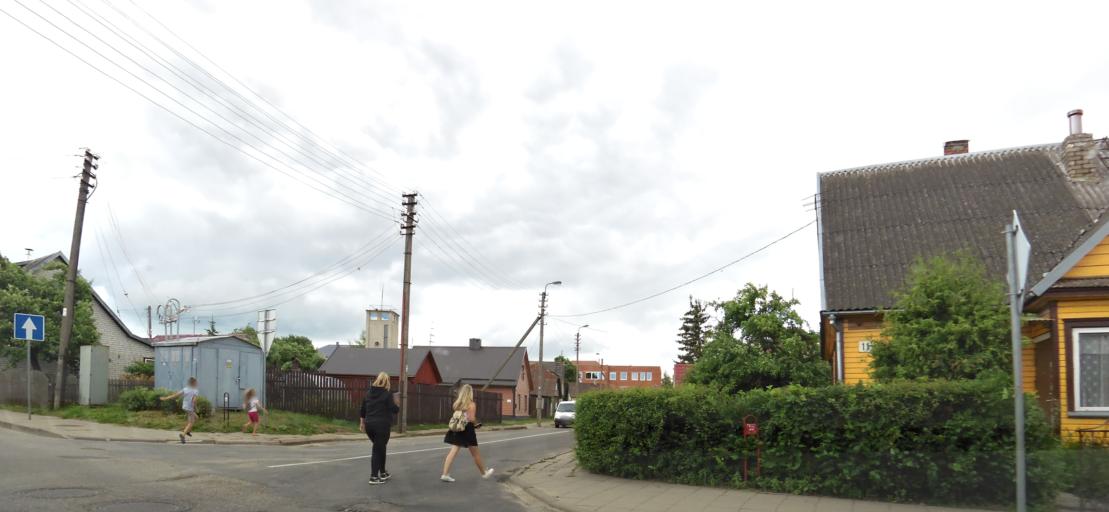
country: LT
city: Kupiskis
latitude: 55.8403
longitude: 24.9728
